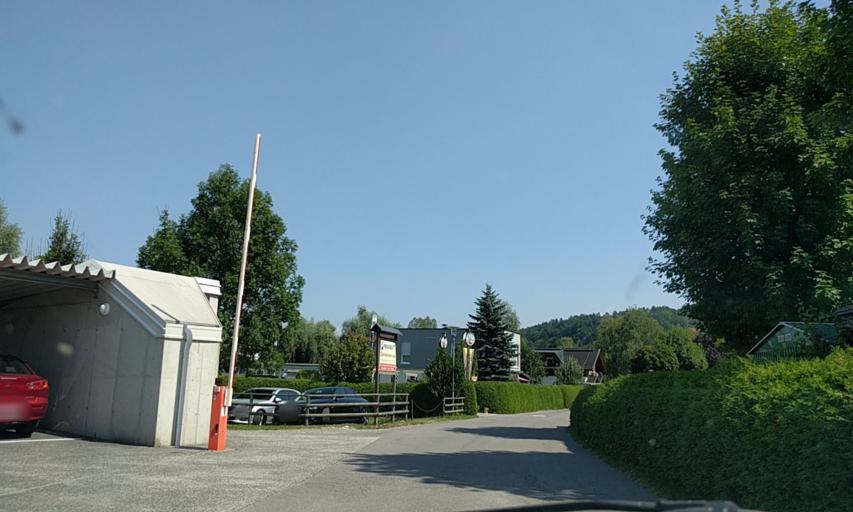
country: AT
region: Carinthia
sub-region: Politischer Bezirk Villach Land
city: Finkenstein am Faaker See
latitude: 46.5666
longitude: 13.9126
